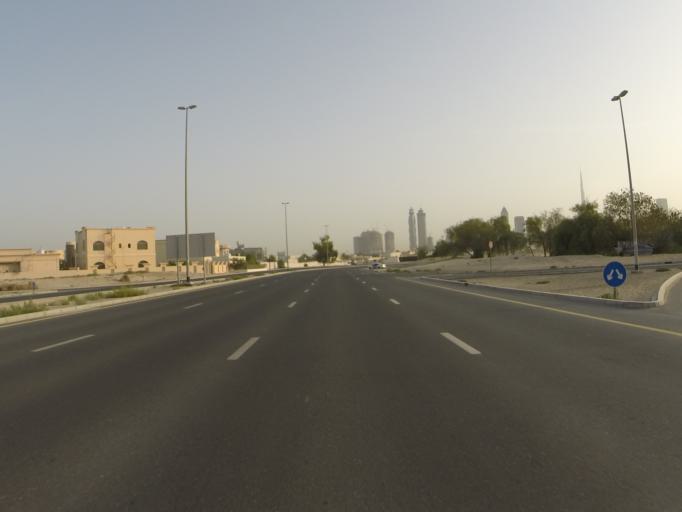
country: AE
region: Dubai
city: Dubai
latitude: 25.1604
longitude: 55.2568
